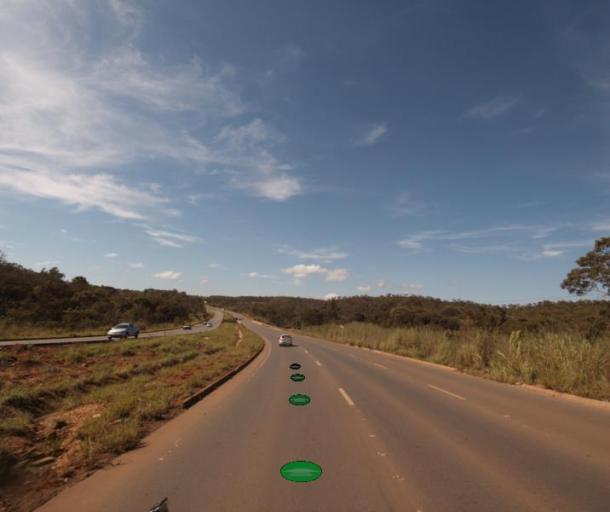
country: BR
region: Federal District
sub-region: Brasilia
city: Brasilia
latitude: -15.7823
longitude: -48.2339
